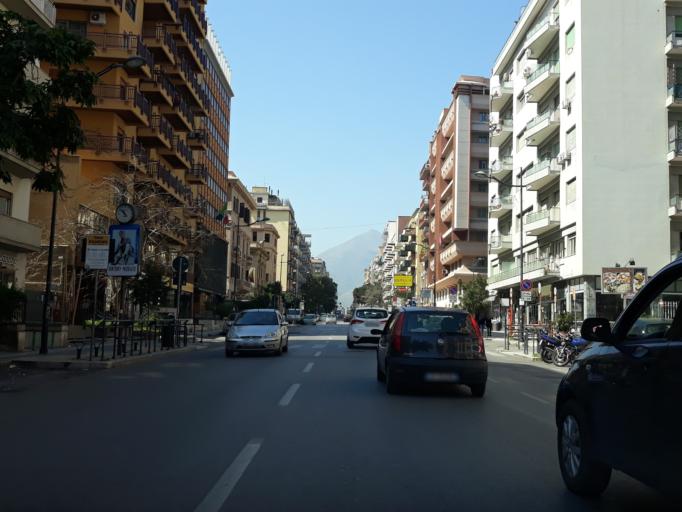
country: IT
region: Sicily
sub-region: Palermo
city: Palermo
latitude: 38.1335
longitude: 13.3490
